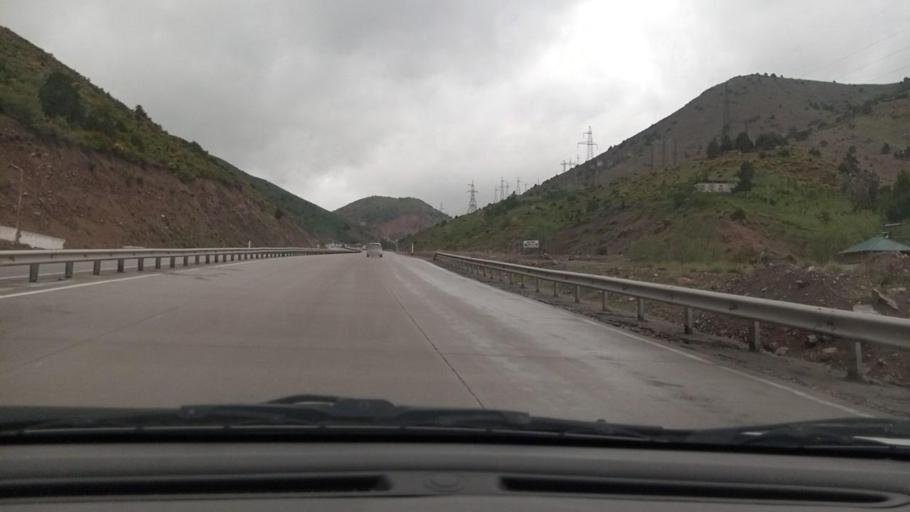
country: UZ
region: Toshkent
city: Angren
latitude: 41.0513
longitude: 70.5678
